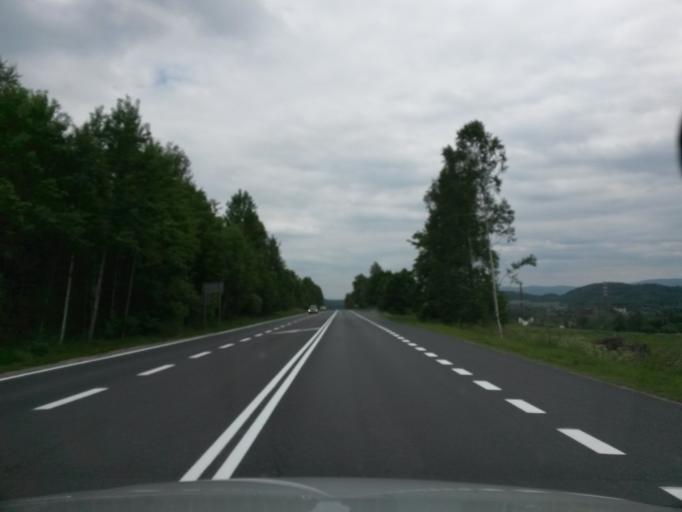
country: PL
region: Lower Silesian Voivodeship
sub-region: Jelenia Gora
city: Cieplice Slaskie Zdroj
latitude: 50.8926
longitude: 15.6941
